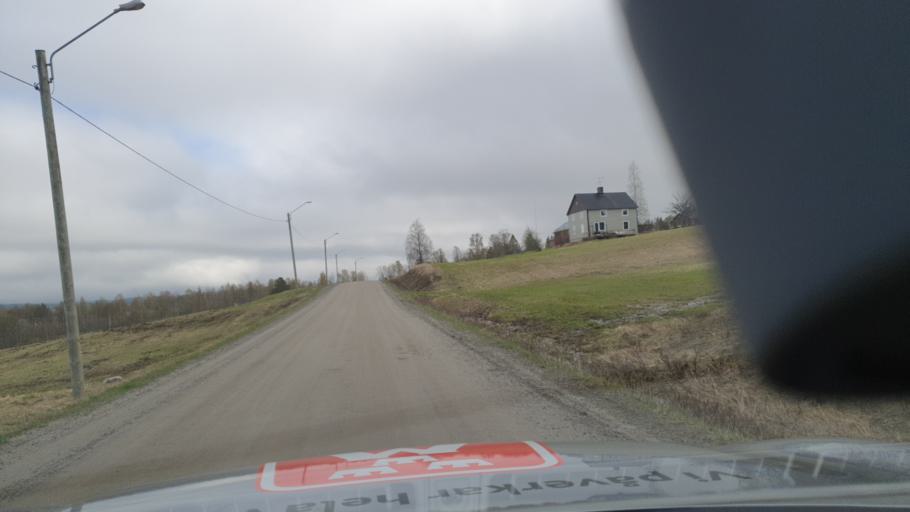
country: SE
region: Vaesterbotten
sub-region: Bjurholms Kommun
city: Bjurholm
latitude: 63.6658
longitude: 19.0144
